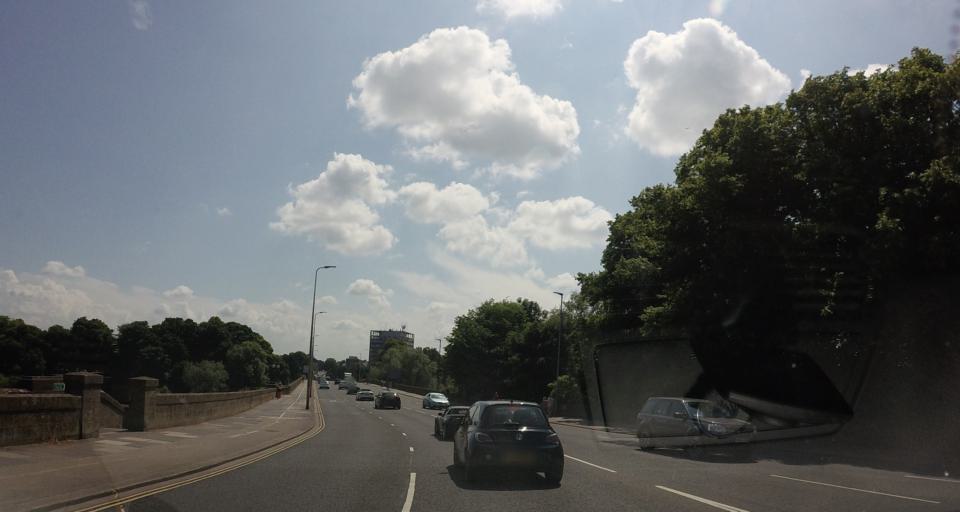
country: GB
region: England
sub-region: Cumbria
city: Carlisle
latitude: 54.9013
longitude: -2.9372
